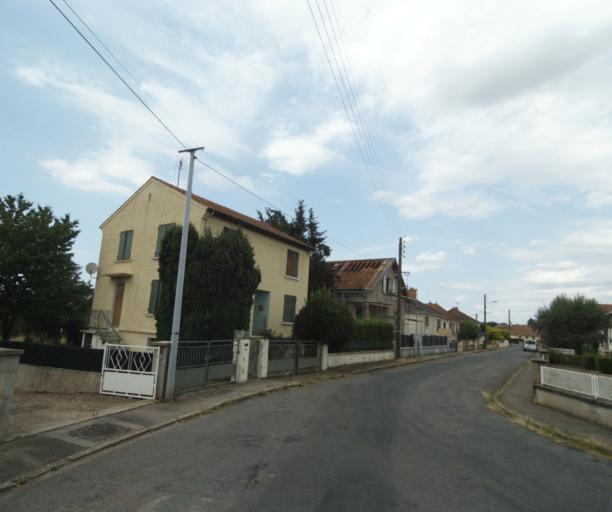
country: FR
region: Bourgogne
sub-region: Departement de Saone-et-Loire
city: Gueugnon
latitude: 46.6043
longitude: 4.0583
